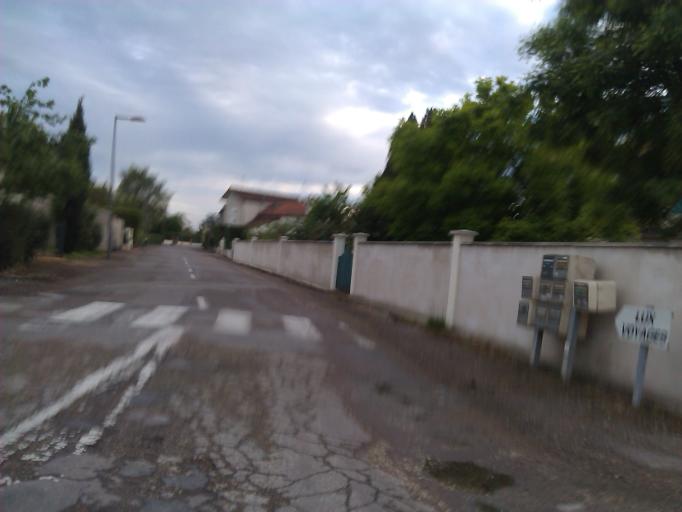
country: FR
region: Bourgogne
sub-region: Departement de Saone-et-Loire
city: Saint-Remy
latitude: 46.7535
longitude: 4.8463
